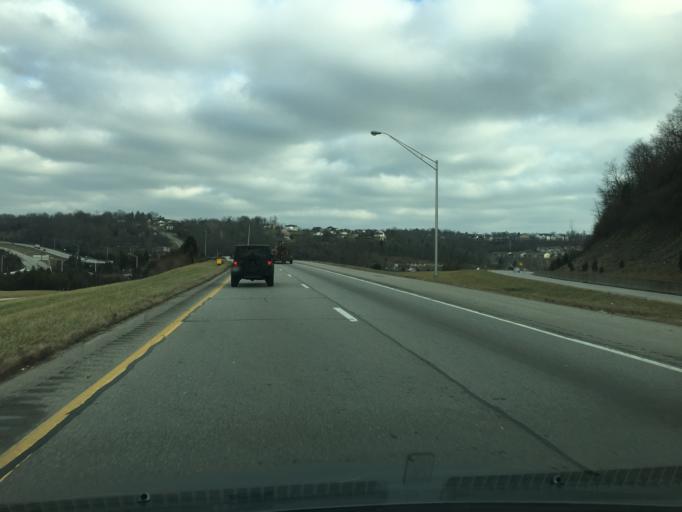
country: US
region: Ohio
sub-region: Hamilton County
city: Miamitown
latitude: 39.2145
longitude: -84.6822
